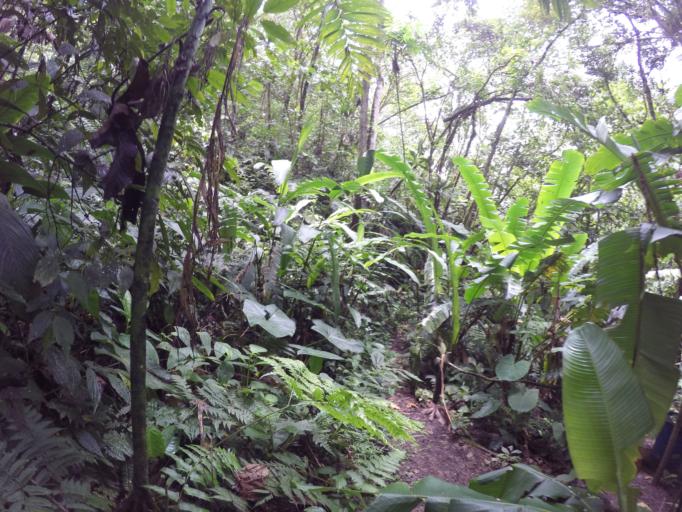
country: CO
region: Quindio
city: Filandia
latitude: 4.7083
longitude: -75.6742
